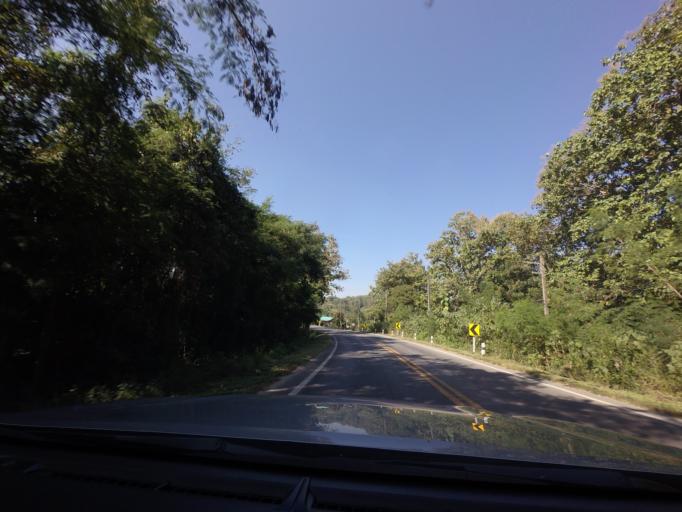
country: TH
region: Sukhothai
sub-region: Amphoe Si Satchanalai
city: Si Satchanalai
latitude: 17.6162
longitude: 99.7090
